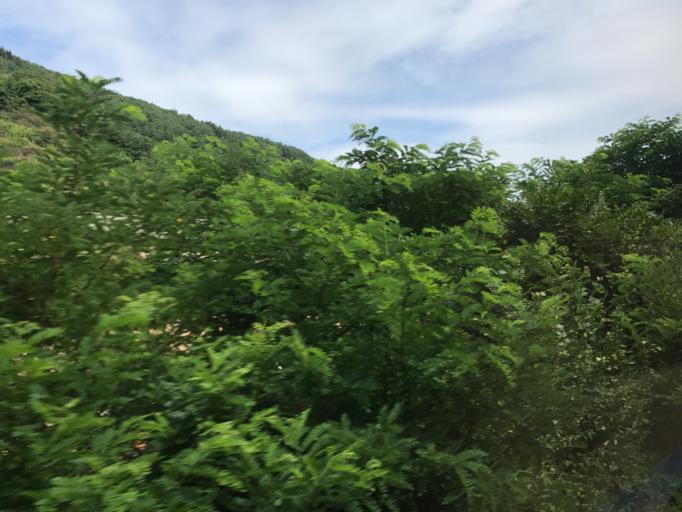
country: DE
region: Rheinland-Pfalz
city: Dienethal
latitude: 50.3160
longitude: 7.7819
